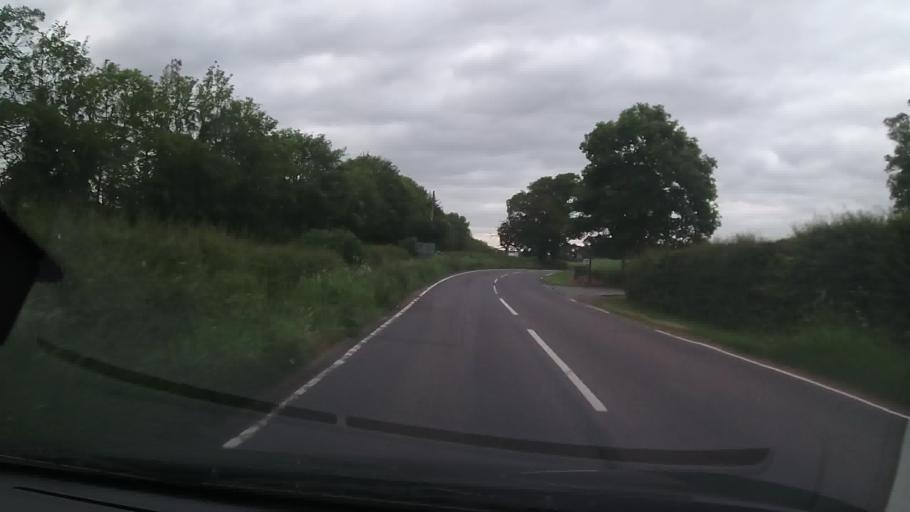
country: GB
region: England
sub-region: Shropshire
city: Clive
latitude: 52.8217
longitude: -2.7395
